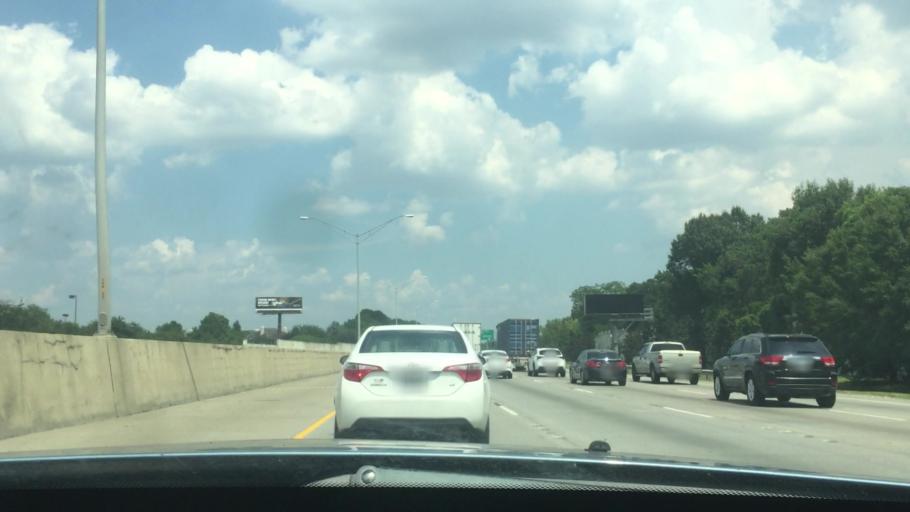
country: US
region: Louisiana
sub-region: East Baton Rouge Parish
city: Baton Rouge
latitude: 30.4217
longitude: -91.1282
